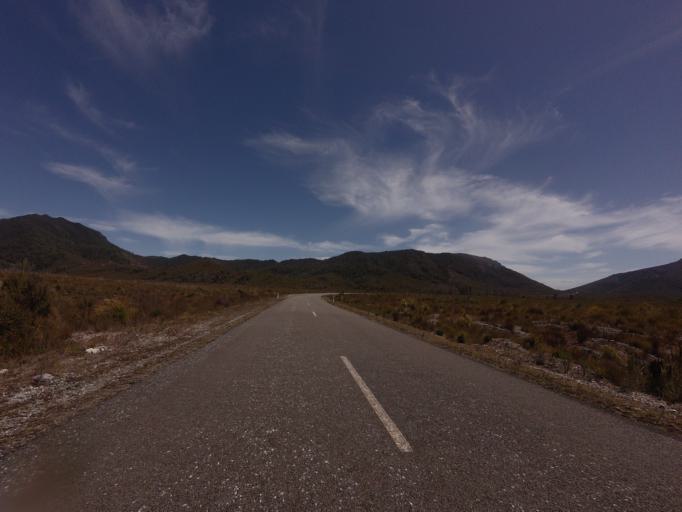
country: AU
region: Tasmania
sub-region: Huon Valley
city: Geeveston
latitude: -42.8626
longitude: 146.2046
